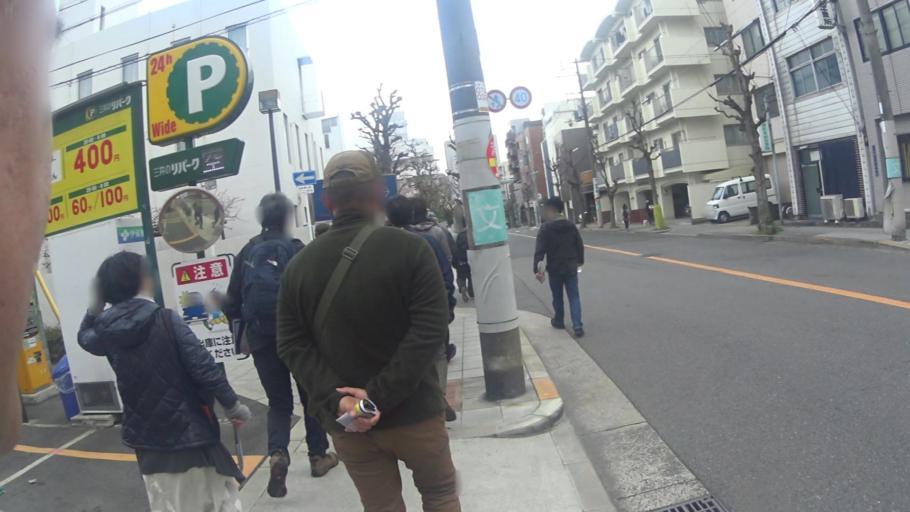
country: JP
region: Osaka
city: Osaka-shi
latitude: 34.6779
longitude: 135.5274
